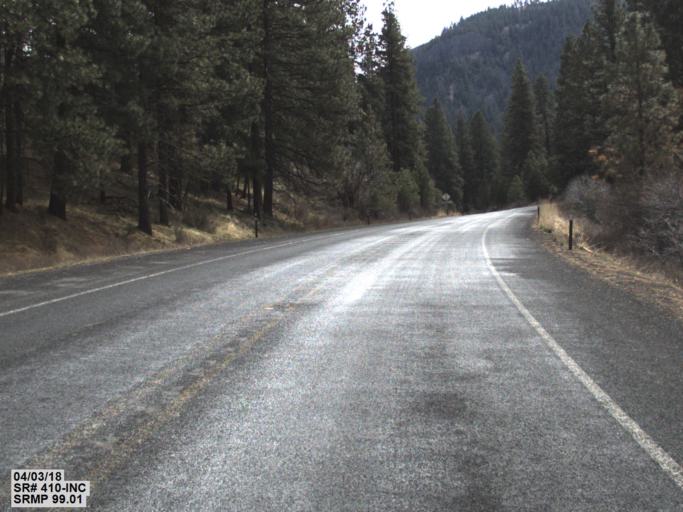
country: US
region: Washington
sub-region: Kittitas County
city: Cle Elum
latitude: 46.9108
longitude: -121.0300
